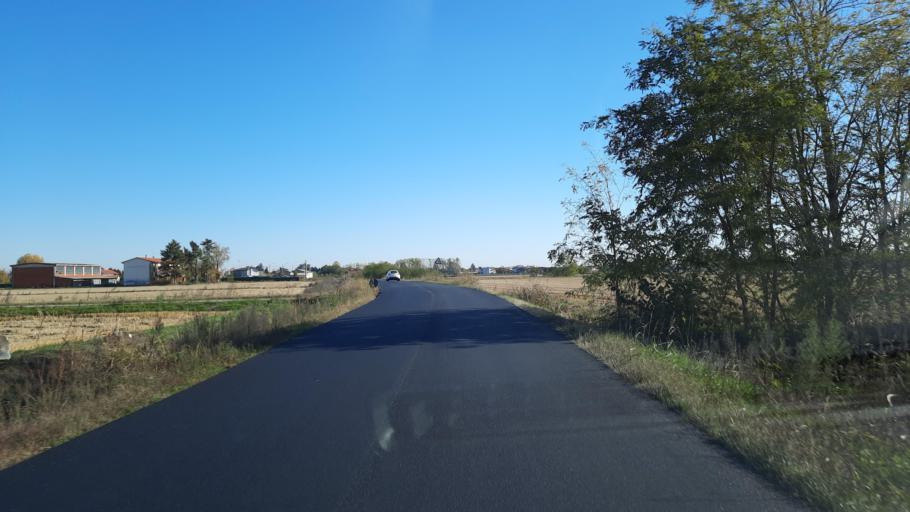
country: IT
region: Piedmont
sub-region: Provincia di Alessandria
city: Villanova Monferrato
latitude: 45.1794
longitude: 8.4631
